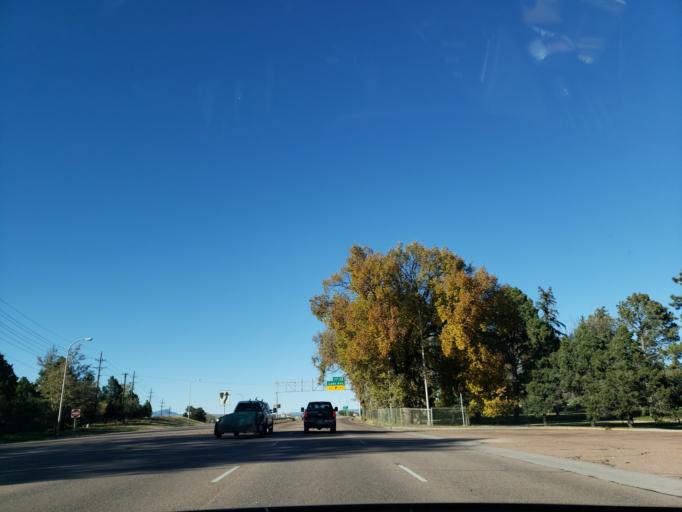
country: US
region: Colorado
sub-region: El Paso County
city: Colorado Springs
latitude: 38.7929
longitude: -104.8220
